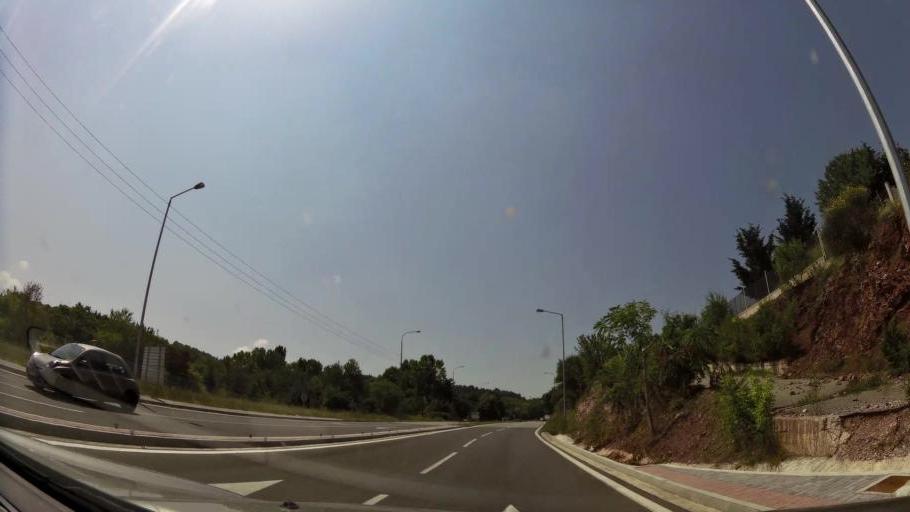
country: GR
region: West Macedonia
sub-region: Nomos Kozanis
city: Koila
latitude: 40.3210
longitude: 21.7882
